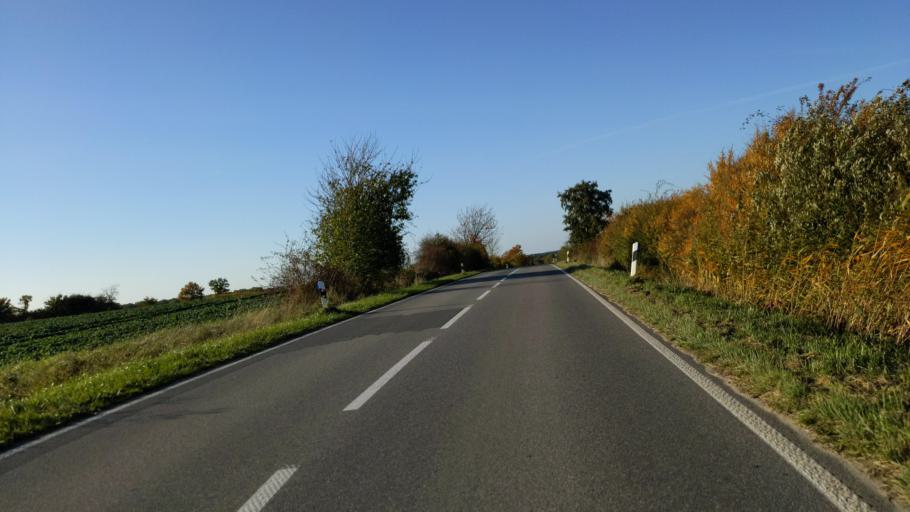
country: DE
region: Schleswig-Holstein
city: Gross Sarau
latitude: 53.7703
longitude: 10.7274
